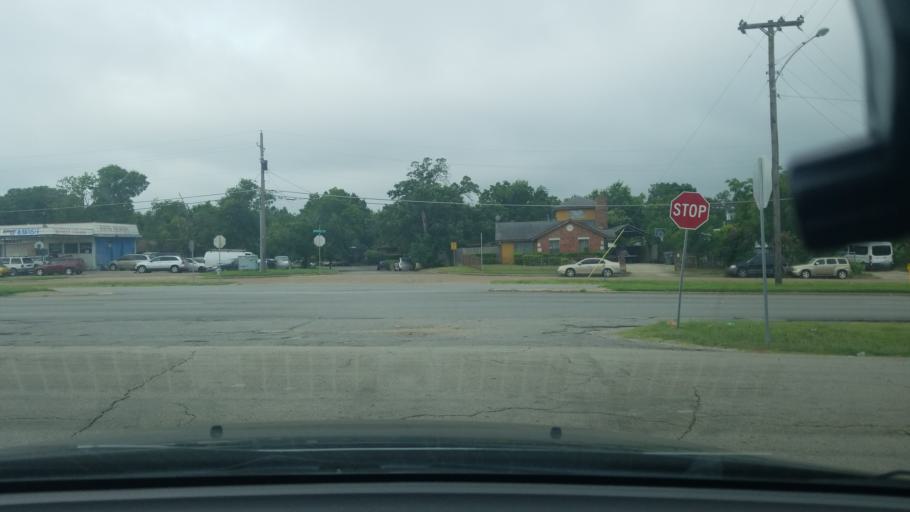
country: US
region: Texas
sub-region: Dallas County
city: Balch Springs
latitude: 32.7715
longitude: -96.6919
